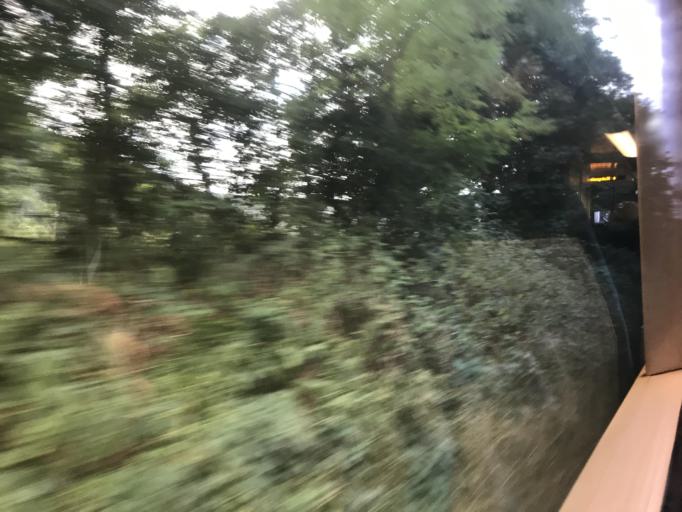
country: DE
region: Bavaria
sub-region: Regierungsbezirk Unterfranken
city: Gemunden
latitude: 50.0641
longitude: 9.6963
